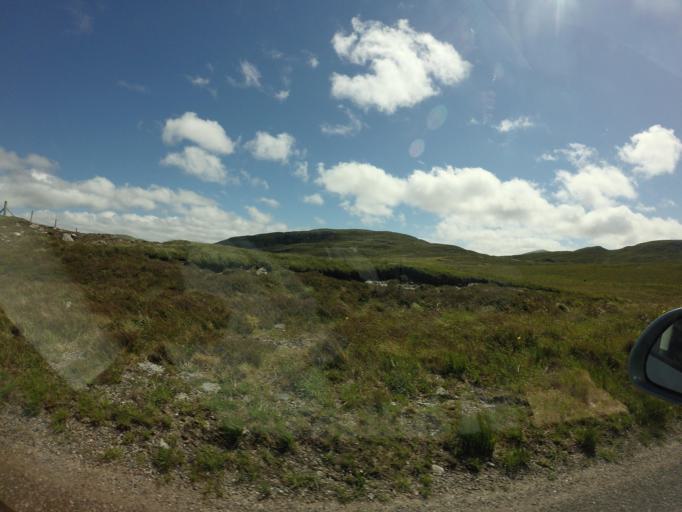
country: GB
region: Scotland
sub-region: Eilean Siar
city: Harris
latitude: 58.0820
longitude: -6.6455
